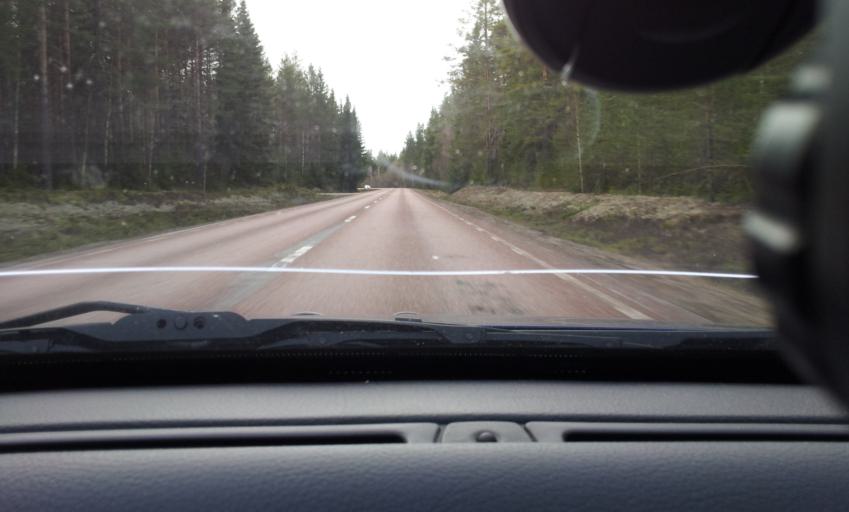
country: SE
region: Gaevleborg
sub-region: Ljusdals Kommun
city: Farila
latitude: 61.8816
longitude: 15.7094
